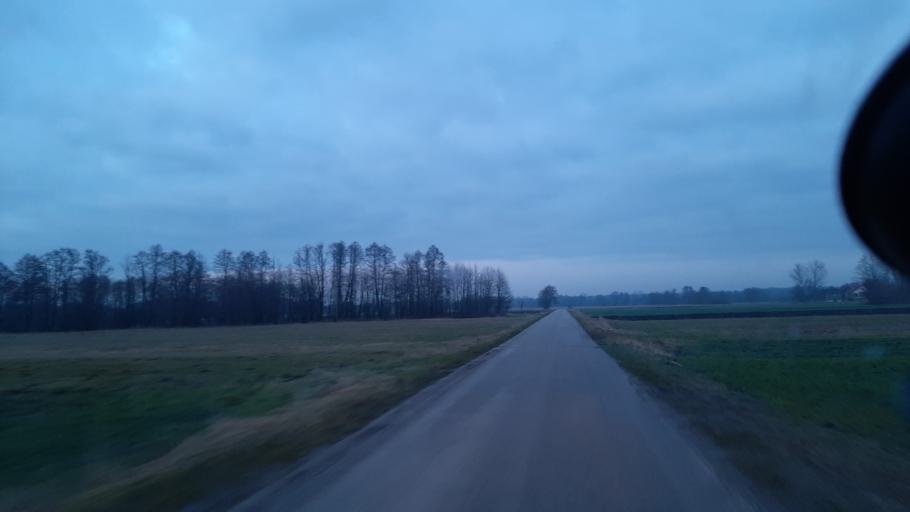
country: PL
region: Lublin Voivodeship
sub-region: Powiat lubartowski
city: Firlej
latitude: 51.5819
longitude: 22.5420
